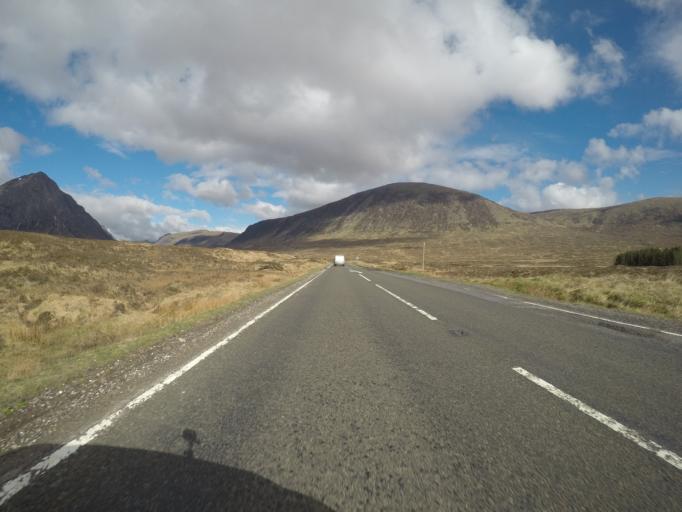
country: GB
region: Scotland
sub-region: Highland
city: Spean Bridge
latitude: 56.6486
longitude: -4.8453
